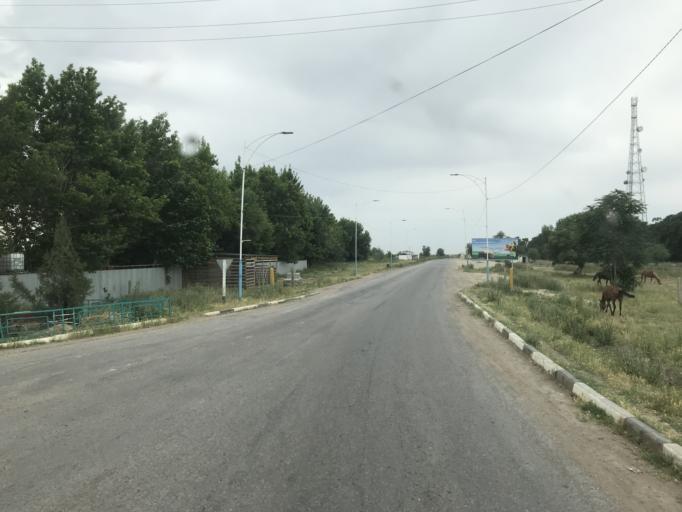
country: KZ
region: Ongtustik Qazaqstan
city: Ilyich
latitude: 40.9565
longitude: 68.4639
